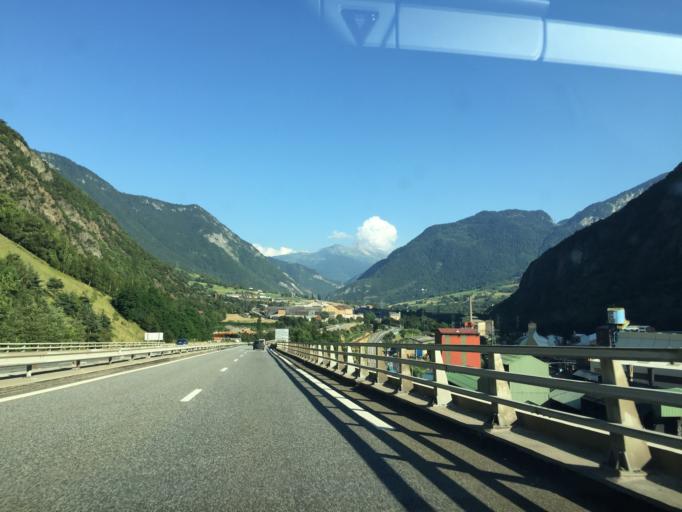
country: FR
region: Rhone-Alpes
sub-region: Departement de la Savoie
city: Aigueblanche
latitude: 45.5301
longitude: 6.4773
